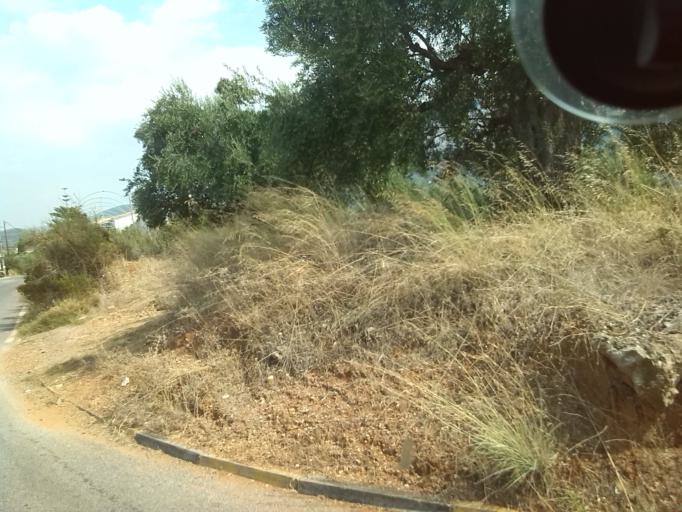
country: GR
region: Peloponnese
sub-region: Nomos Messinias
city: Kyparissia
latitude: 37.2653
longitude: 21.6890
